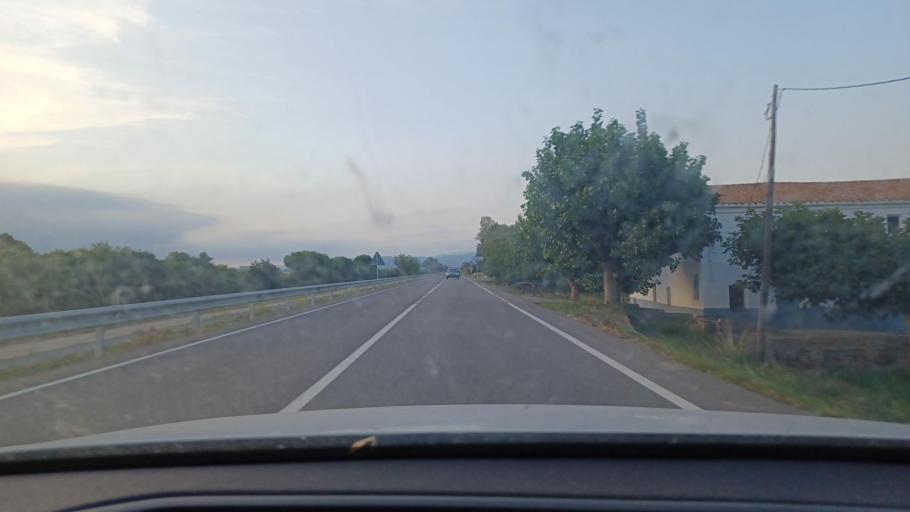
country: ES
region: Catalonia
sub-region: Provincia de Tarragona
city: Amposta
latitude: 40.6718
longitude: 0.5906
